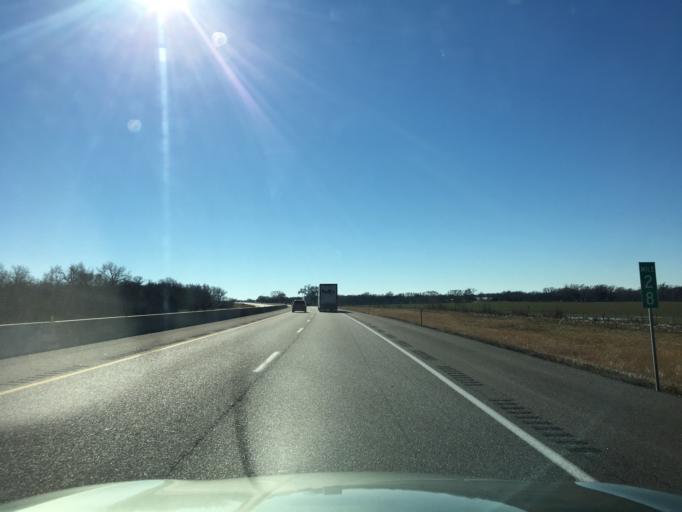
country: US
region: Kansas
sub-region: Sumner County
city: Belle Plaine
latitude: 37.3993
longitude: -97.3258
